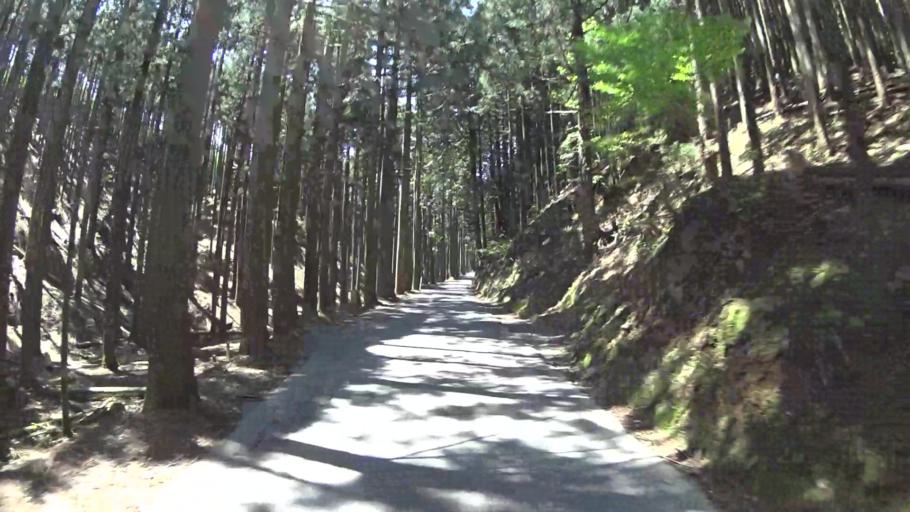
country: JP
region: Shiga Prefecture
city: Kitahama
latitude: 35.1552
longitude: 135.7988
